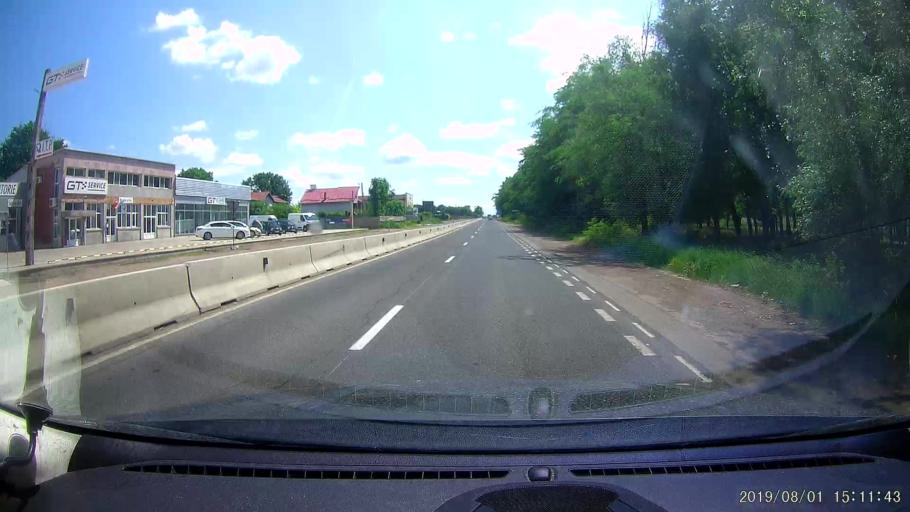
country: RO
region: Braila
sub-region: Comuna Chiscani
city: Chiscani
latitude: 45.2151
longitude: 27.9217
